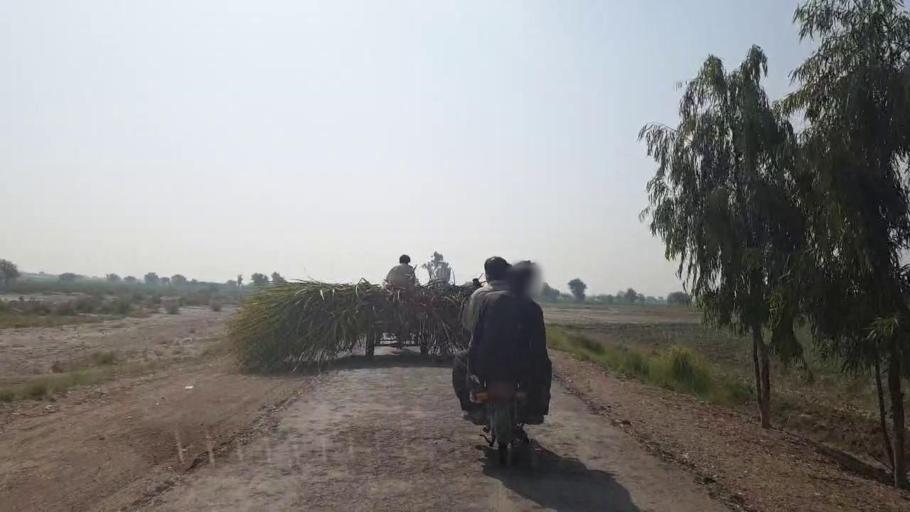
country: PK
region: Sindh
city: Shahdadpur
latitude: 25.9267
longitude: 68.7334
